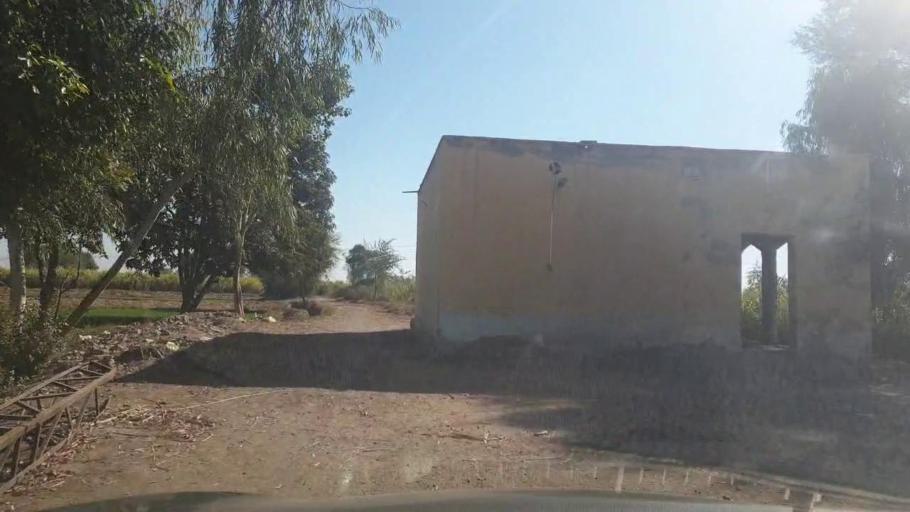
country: PK
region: Sindh
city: Adilpur
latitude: 27.9667
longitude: 69.3338
